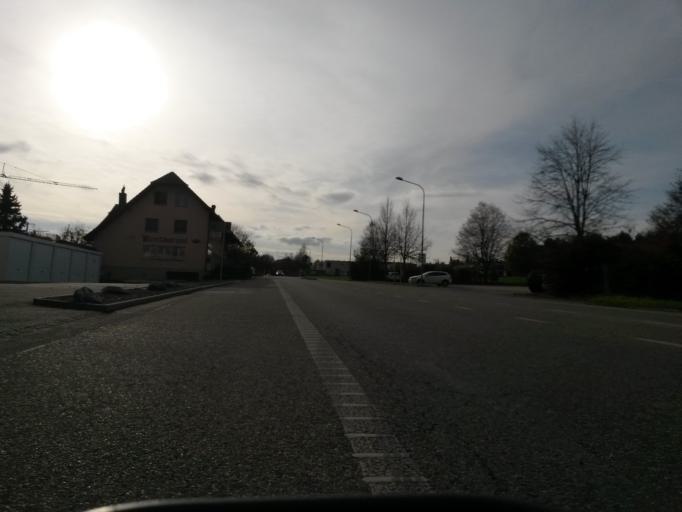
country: CH
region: Solothurn
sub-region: Bezirk Wasseramt
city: Biberist
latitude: 47.1746
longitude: 7.5400
